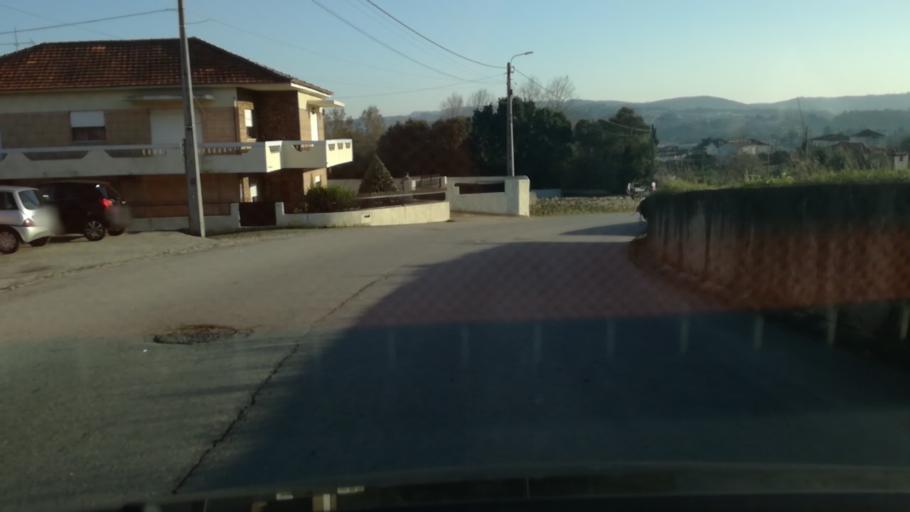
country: PT
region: Braga
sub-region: Vila Nova de Famalicao
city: Ferreiros
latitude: 41.3563
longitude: -8.5292
